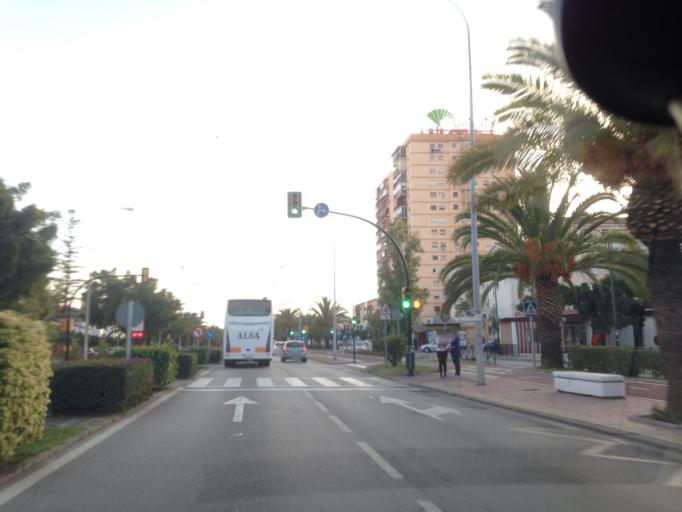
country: ES
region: Andalusia
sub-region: Provincia de Malaga
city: Malaga
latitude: 36.7459
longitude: -4.4227
